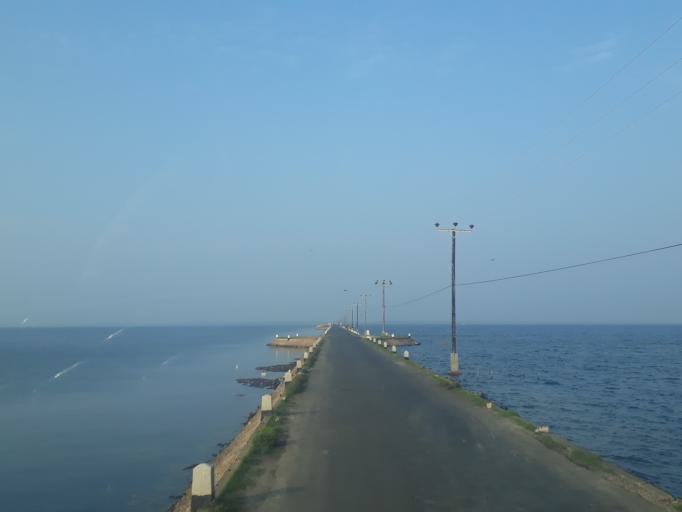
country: LK
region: Northern Province
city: Jaffna
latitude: 9.6228
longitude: 79.8910
